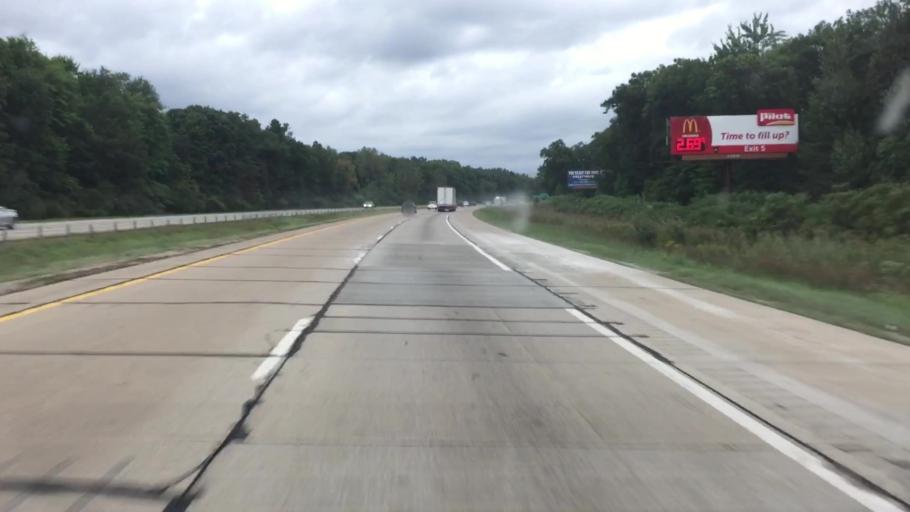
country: US
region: Michigan
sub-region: Monroe County
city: Petersburg
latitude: 41.8544
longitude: -83.6617
